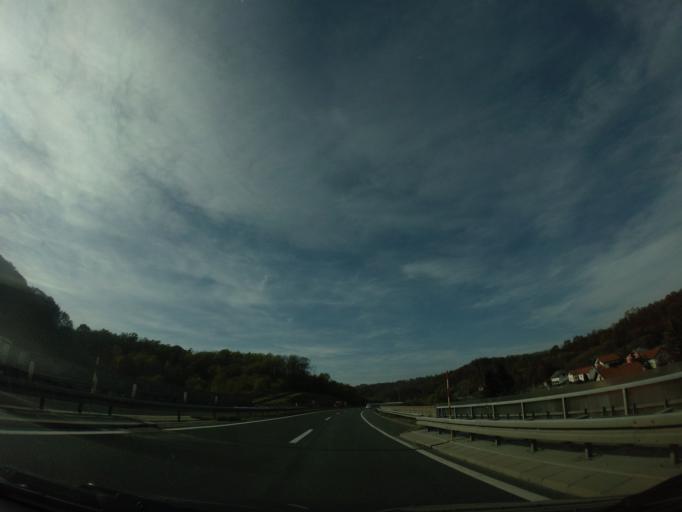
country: HR
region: Varazdinska
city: Remetinec
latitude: 46.1259
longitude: 16.3186
